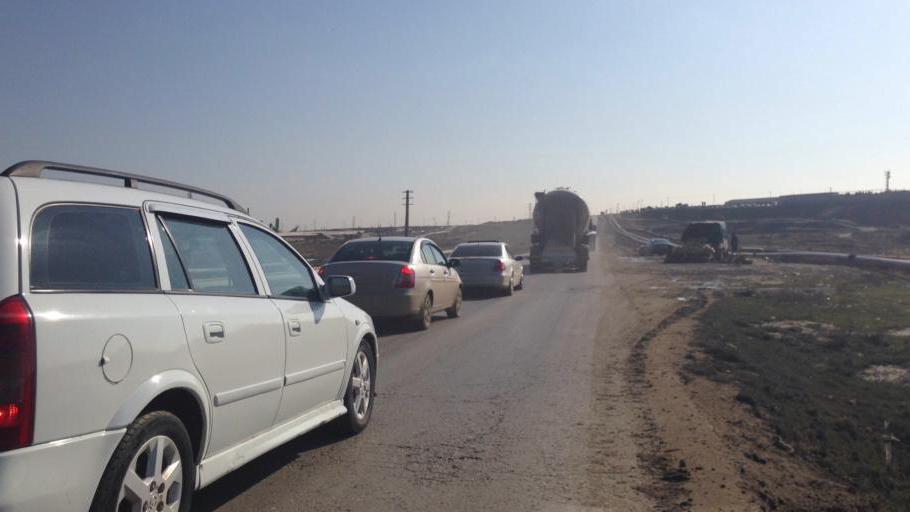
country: AZ
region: Abseron
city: Digah
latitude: 40.4683
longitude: 49.8861
